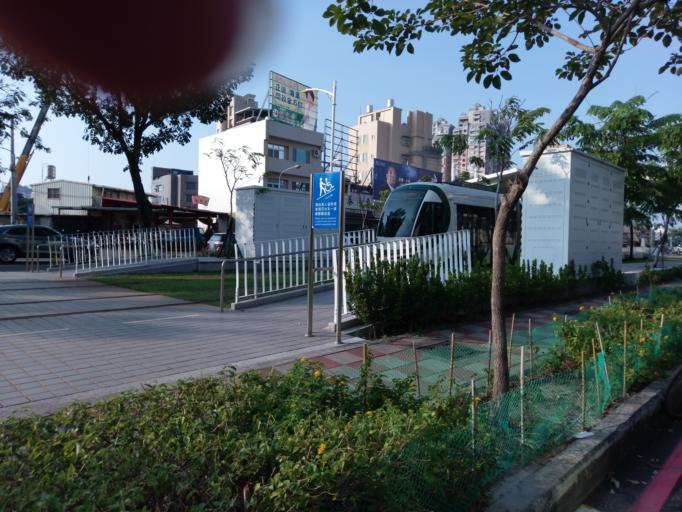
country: TW
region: Kaohsiung
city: Kaohsiung
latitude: 22.6043
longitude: 120.3248
